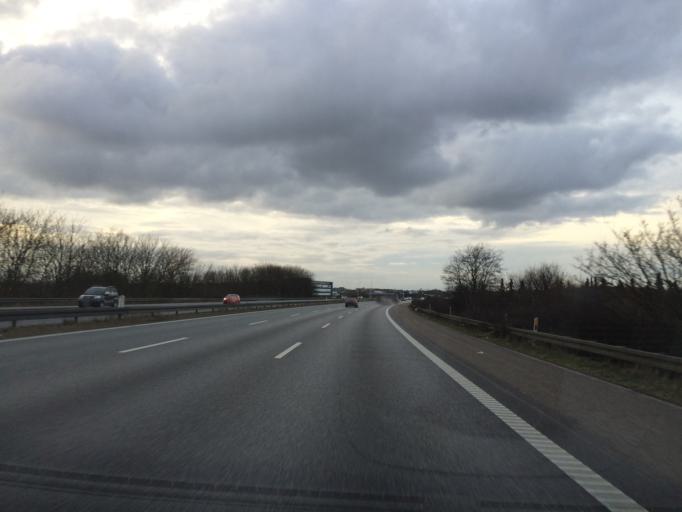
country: DK
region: South Denmark
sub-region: Fredericia Kommune
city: Snoghoj
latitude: 55.5228
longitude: 9.7320
